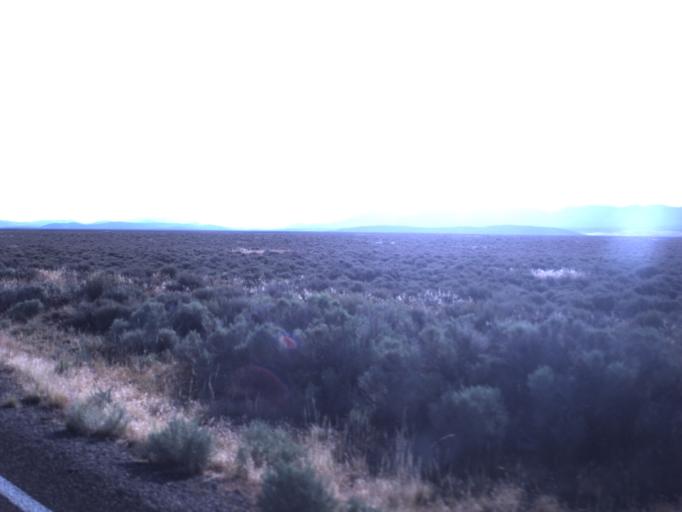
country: US
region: Utah
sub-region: Iron County
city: Enoch
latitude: 37.9430
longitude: -113.0205
